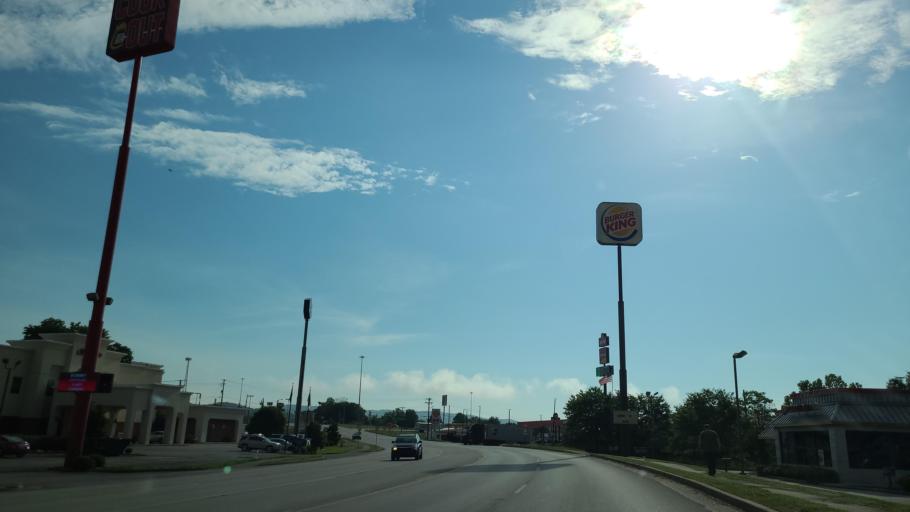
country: US
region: Kentucky
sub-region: Whitley County
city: Williamsburg
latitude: 36.7219
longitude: -84.1701
